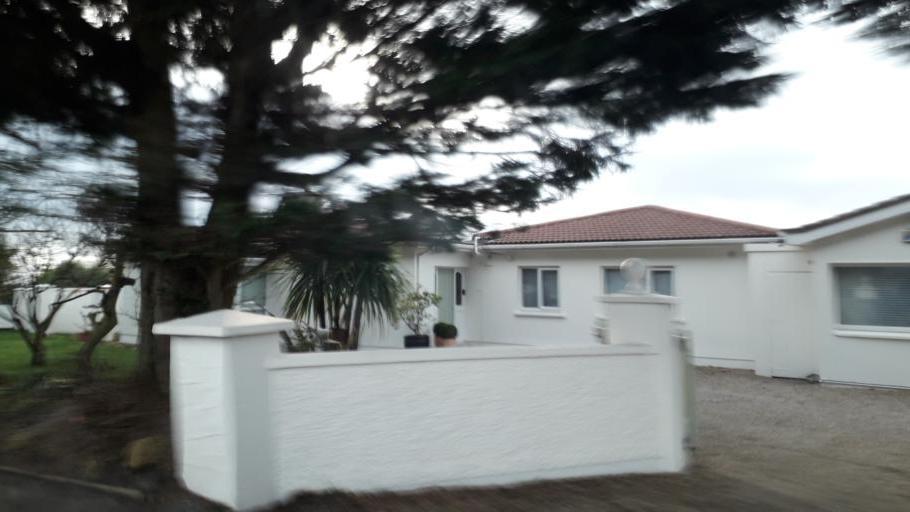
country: IE
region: Leinster
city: An Ros
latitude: 53.5463
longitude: -6.1007
